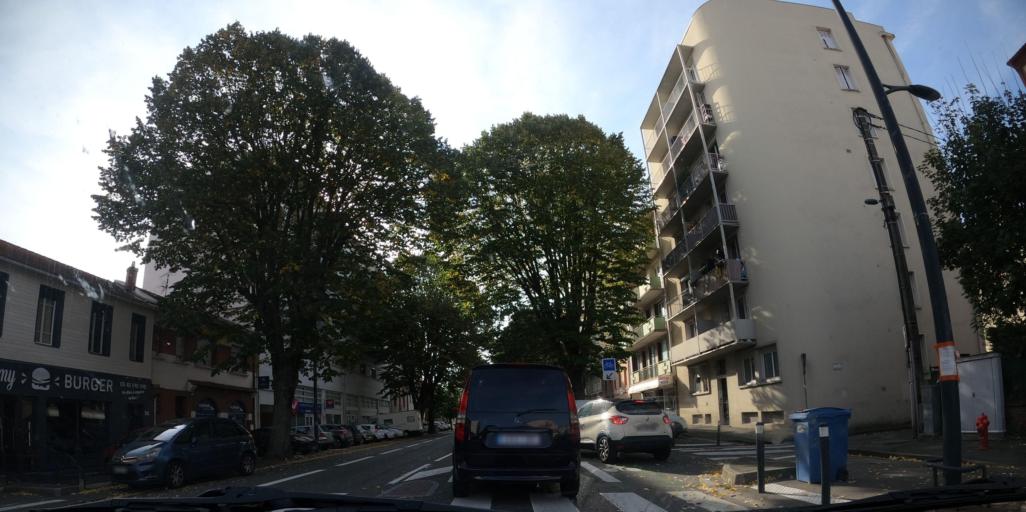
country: FR
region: Midi-Pyrenees
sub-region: Departement de la Haute-Garonne
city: Toulouse
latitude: 43.5761
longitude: 1.4511
